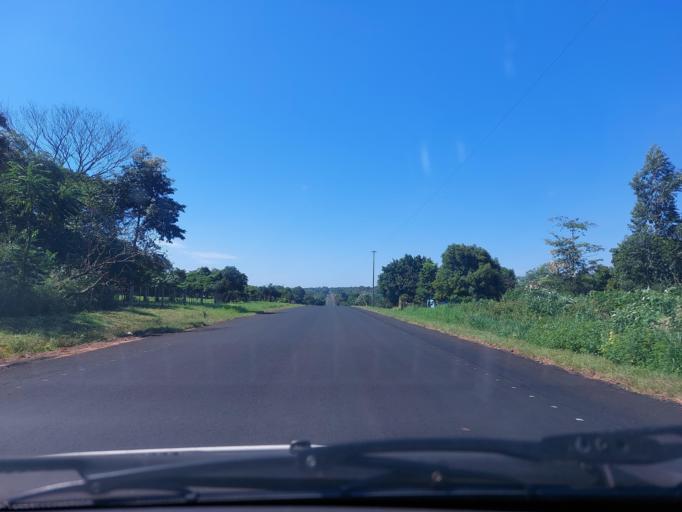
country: PY
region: San Pedro
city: Guayaybi
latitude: -24.5504
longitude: -56.4937
